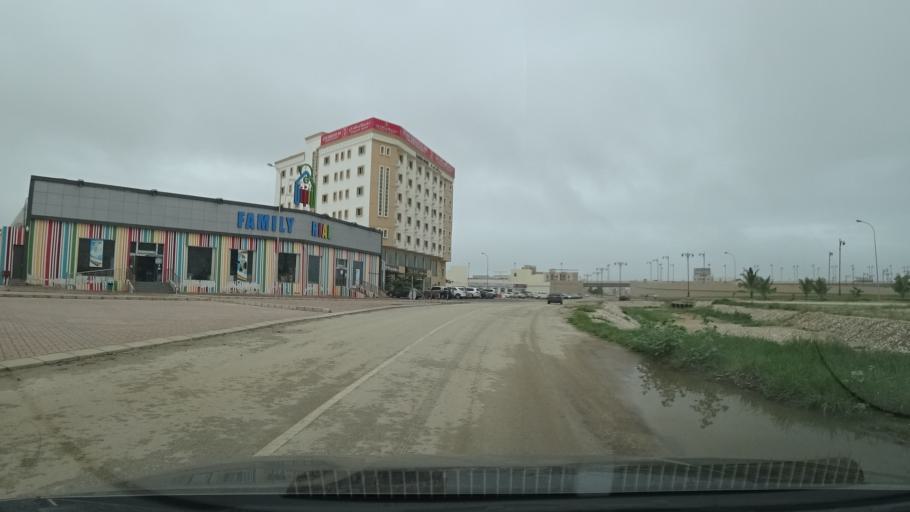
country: OM
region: Zufar
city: Salalah
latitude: 17.0209
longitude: 54.0585
